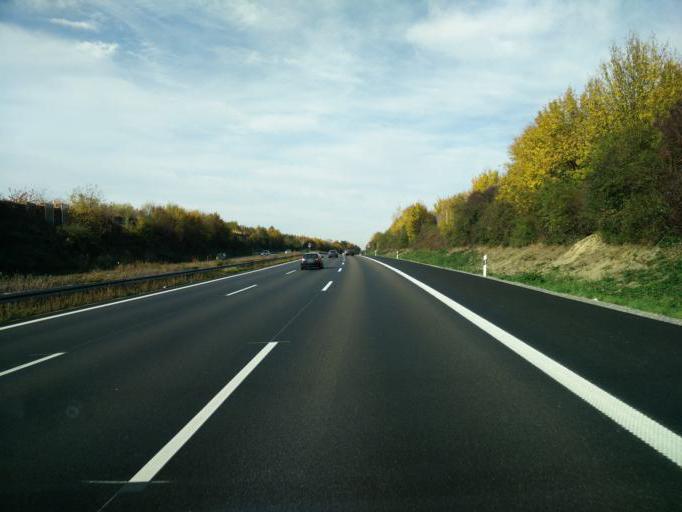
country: DE
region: Baden-Wuerttemberg
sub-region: Karlsruhe Region
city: Ettlingen
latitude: 48.9605
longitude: 8.4757
